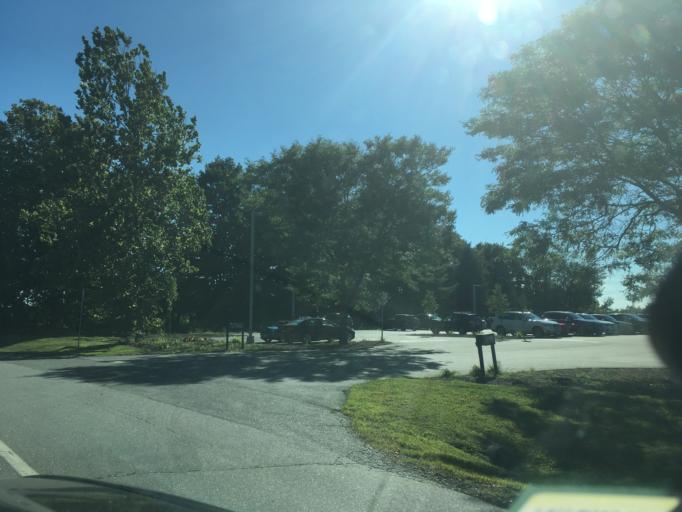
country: US
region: New Hampshire
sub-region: Rockingham County
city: Exeter
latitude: 43.0104
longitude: -70.9183
